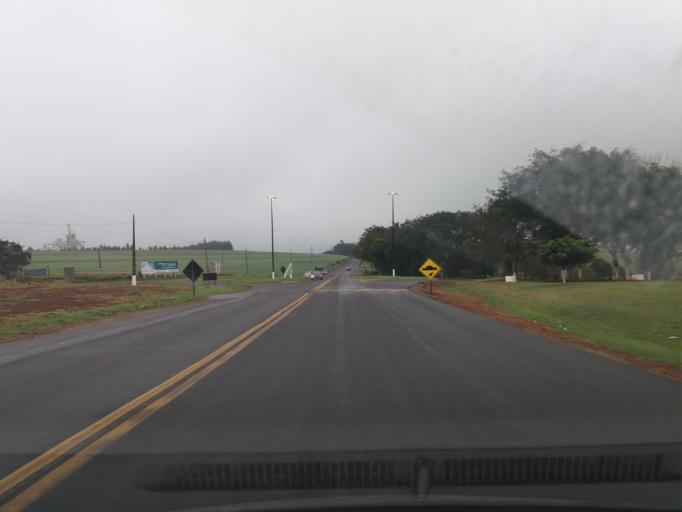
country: BR
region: Parana
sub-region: Ampere
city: Ampere
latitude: -25.9002
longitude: -53.4498
